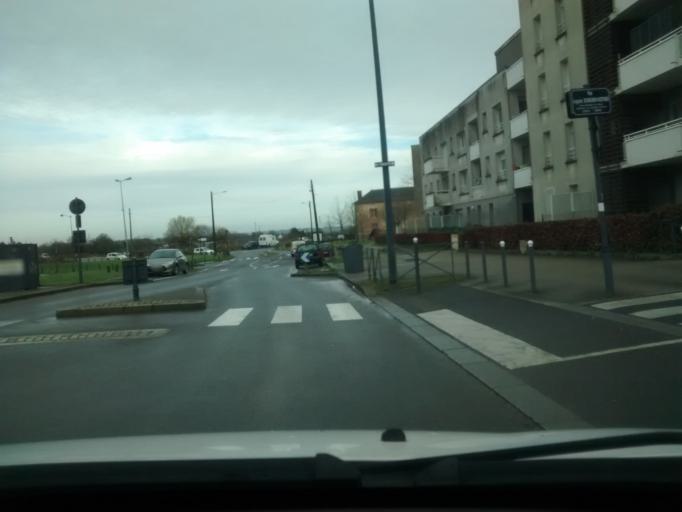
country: FR
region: Brittany
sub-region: Departement d'Ille-et-Vilaine
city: Saint-Gregoire
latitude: 48.1303
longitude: -1.7036
